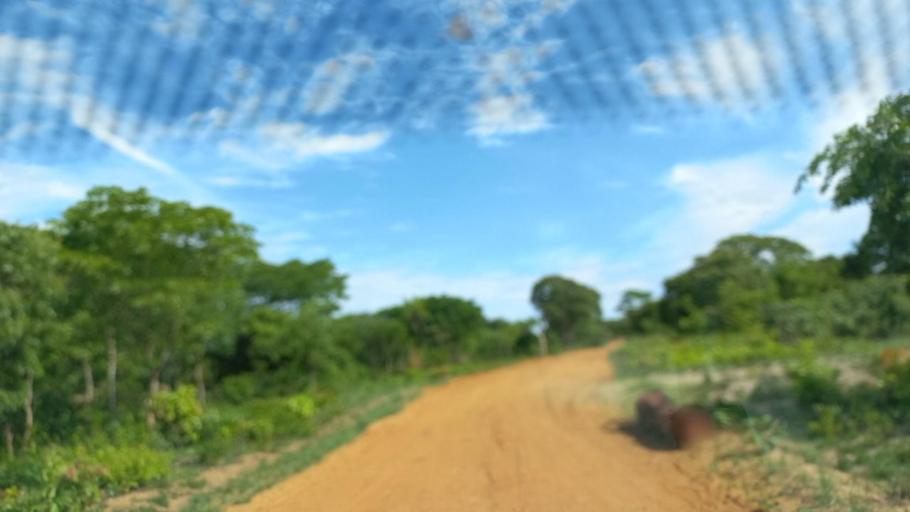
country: ZM
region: North-Western
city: Kabompo
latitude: -13.0724
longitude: 24.2181
